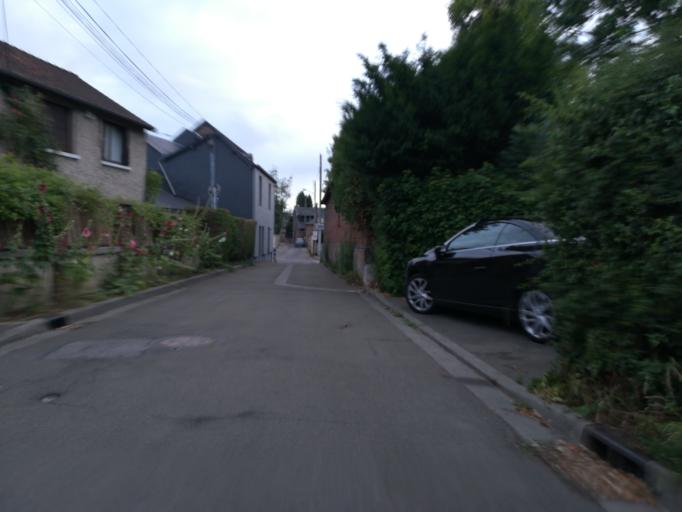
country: FR
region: Haute-Normandie
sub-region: Departement de la Seine-Maritime
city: Mont-Saint-Aignan
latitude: 49.4668
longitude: 1.0860
